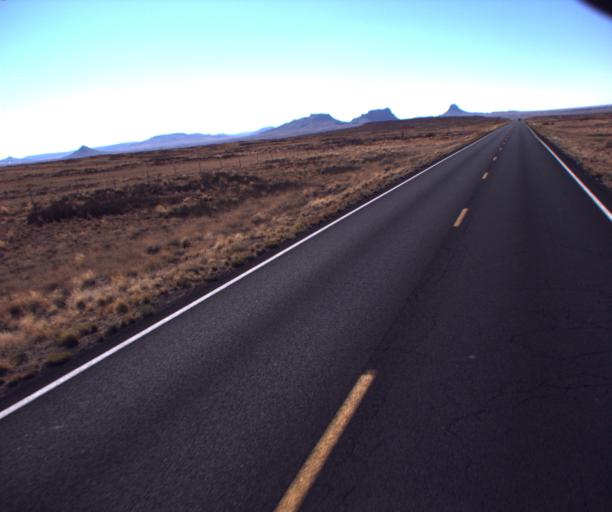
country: US
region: Arizona
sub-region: Navajo County
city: Dilkon
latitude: 35.4042
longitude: -110.4263
